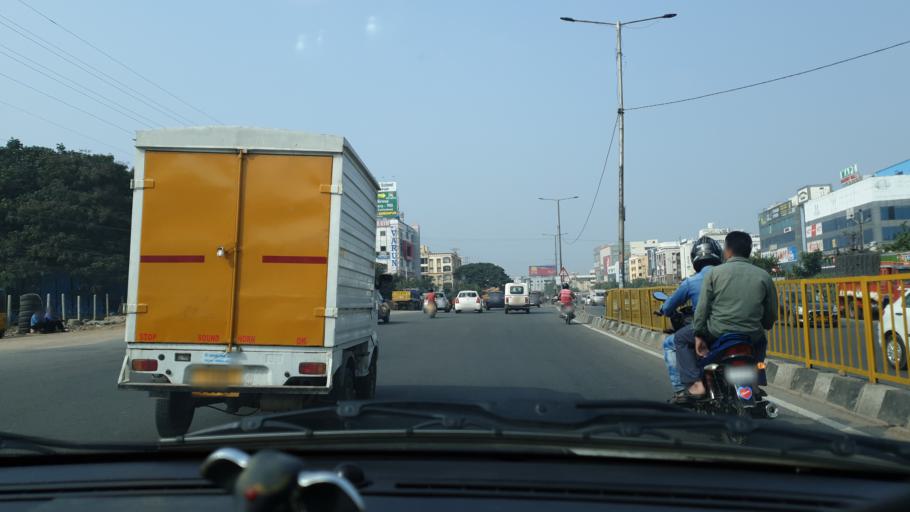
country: IN
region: Telangana
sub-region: Medak
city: Serilingampalle
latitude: 17.4951
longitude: 78.3398
